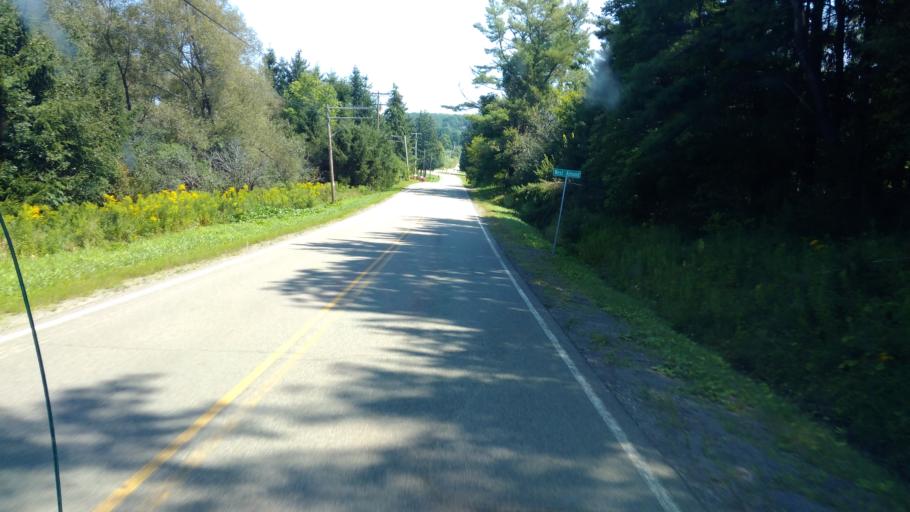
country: US
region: New York
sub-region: Allegany County
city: Alfred
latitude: 42.2990
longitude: -77.8875
